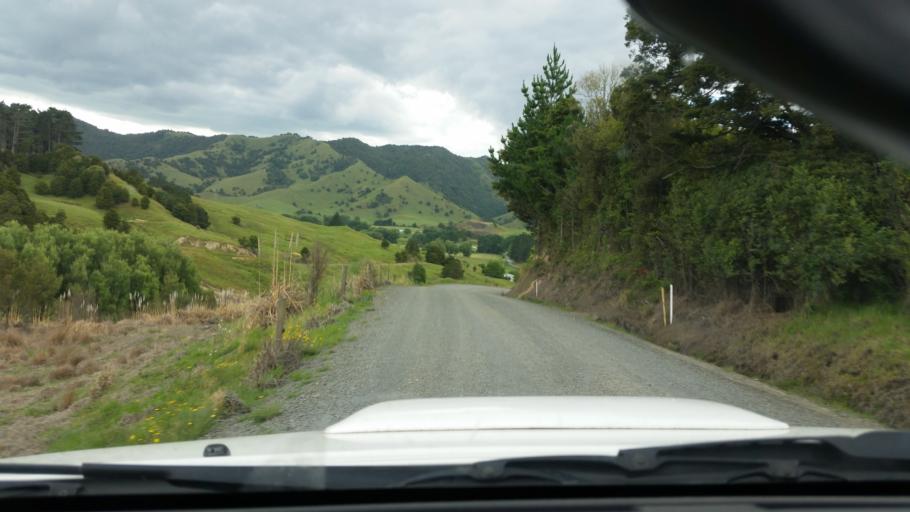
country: NZ
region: Northland
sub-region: Kaipara District
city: Dargaville
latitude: -35.8042
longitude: 173.9031
